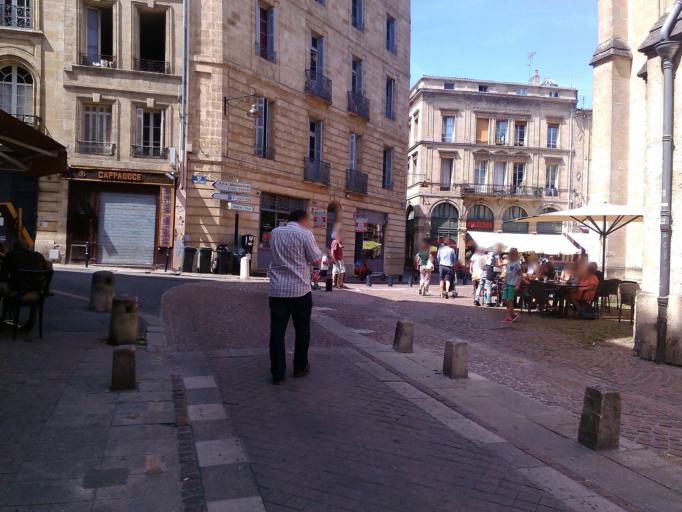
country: FR
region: Aquitaine
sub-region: Departement de la Gironde
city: Bordeaux
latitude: 44.8397
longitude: -0.5703
